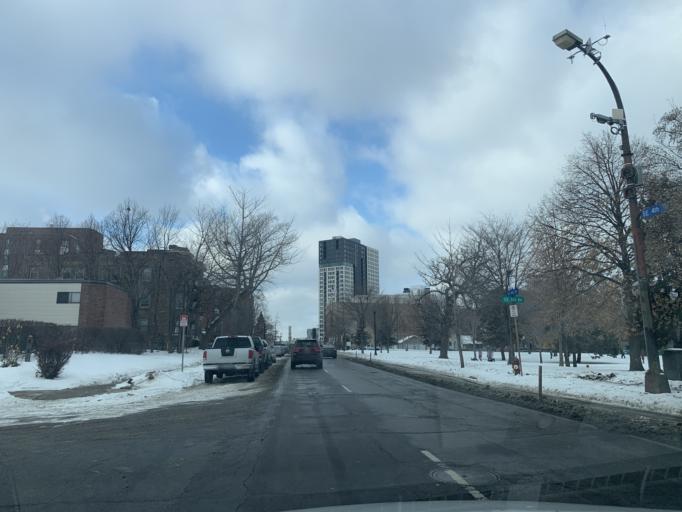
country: US
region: Minnesota
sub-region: Hennepin County
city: Minneapolis
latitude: 44.9866
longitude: -93.2511
